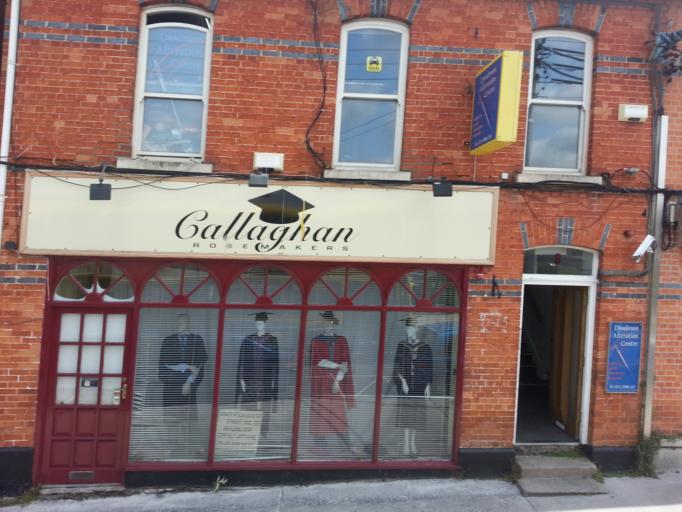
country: IE
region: Leinster
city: Dundrum
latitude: 53.2912
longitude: -6.2456
